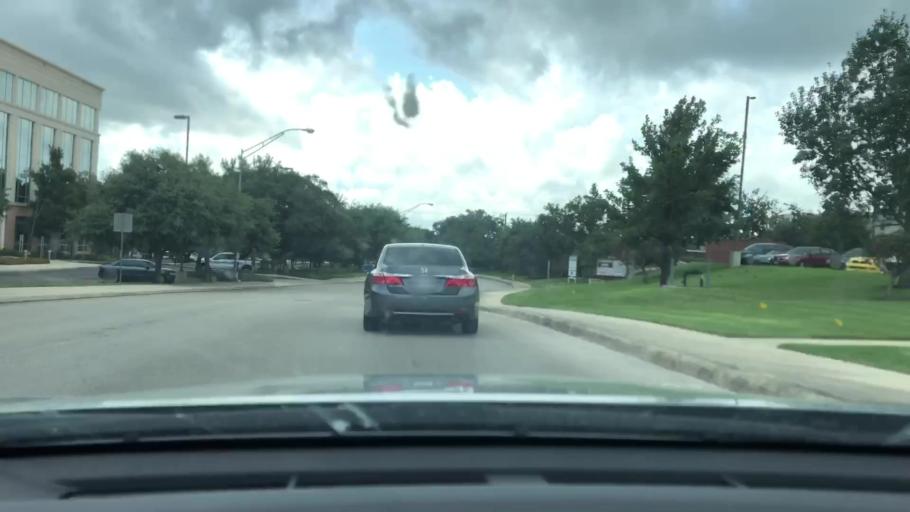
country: US
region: Texas
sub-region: Bexar County
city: Hollywood Park
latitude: 29.6147
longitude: -98.4834
